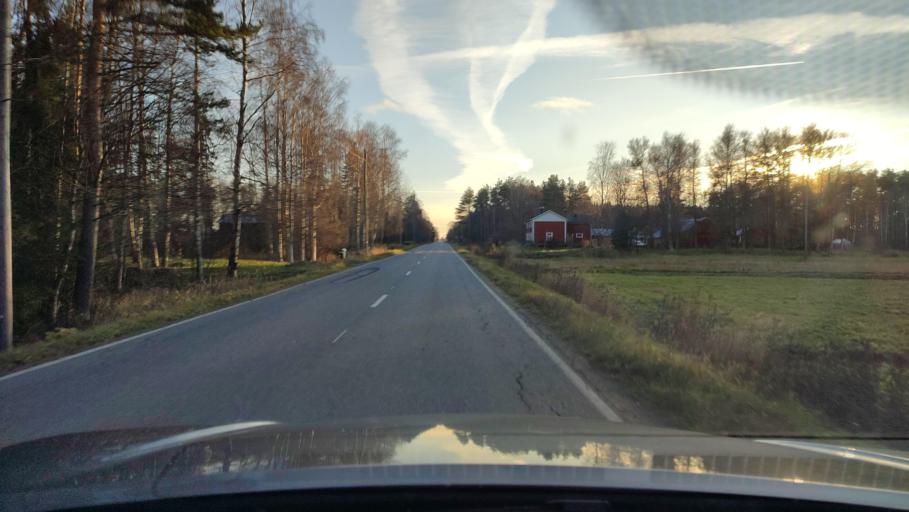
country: FI
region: Ostrobothnia
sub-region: Sydosterbotten
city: Naerpes
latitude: 62.6463
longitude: 21.5080
